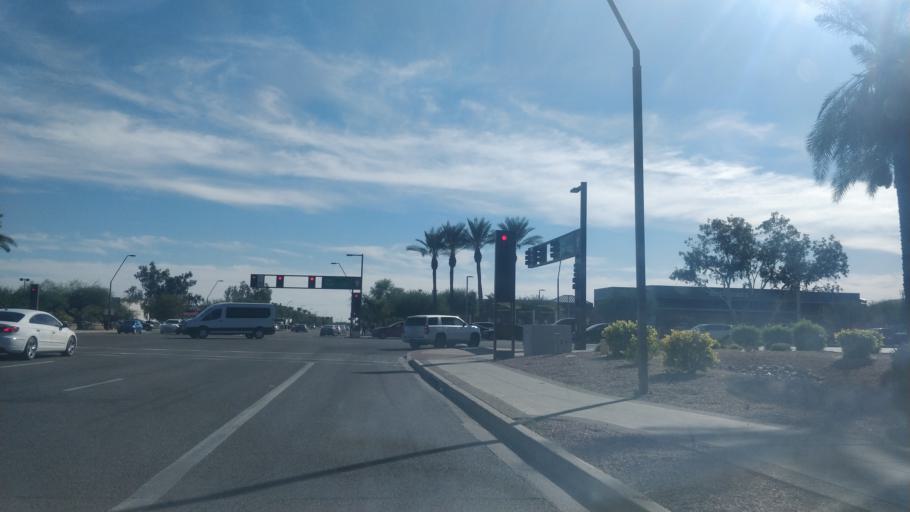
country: US
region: Arizona
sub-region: Maricopa County
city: Guadalupe
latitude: 33.3496
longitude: -111.9633
